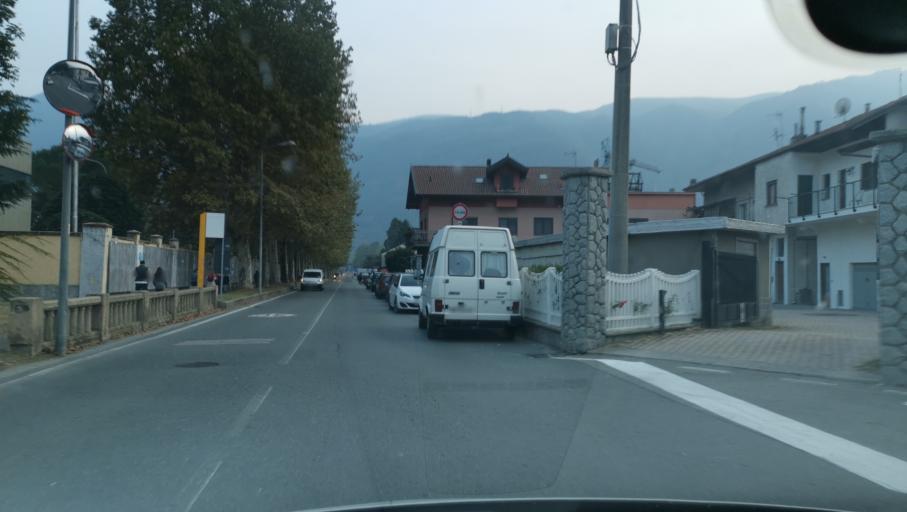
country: IT
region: Piedmont
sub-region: Provincia di Torino
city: Condove
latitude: 45.1129
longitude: 7.3135
